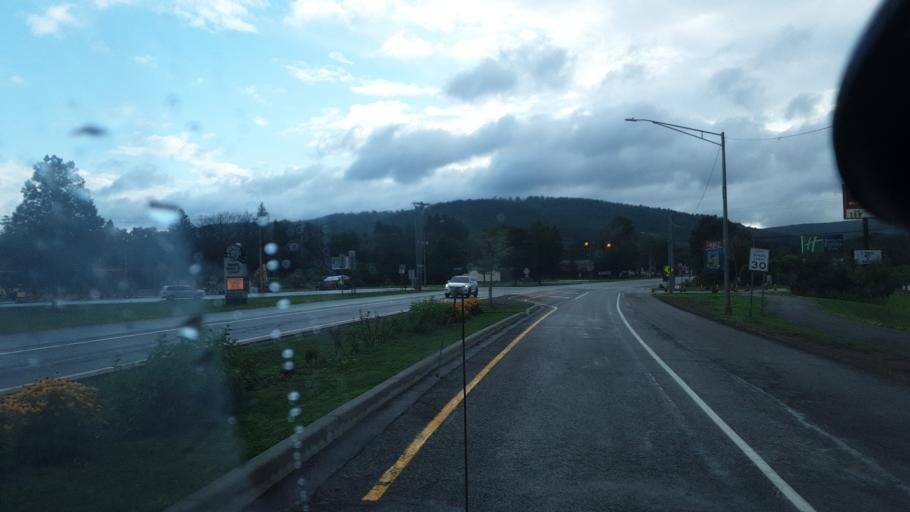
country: US
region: New York
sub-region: Cattaraugus County
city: Salamanca
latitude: 42.1543
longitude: -78.7535
